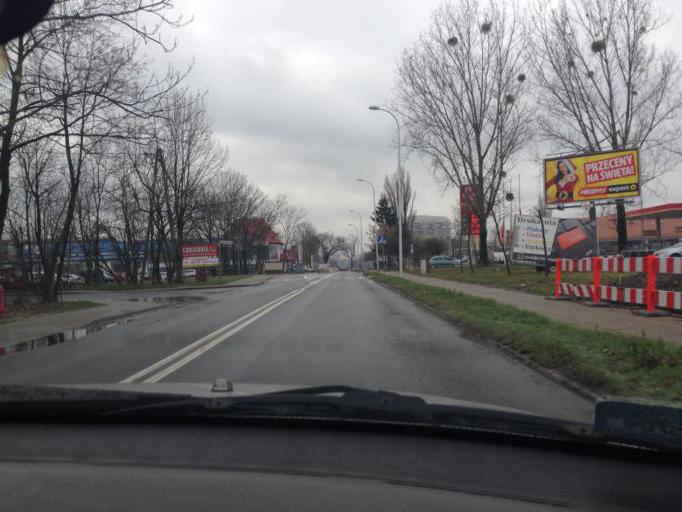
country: PL
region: Opole Voivodeship
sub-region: Powiat opolski
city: Opole
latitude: 50.6813
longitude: 17.9399
